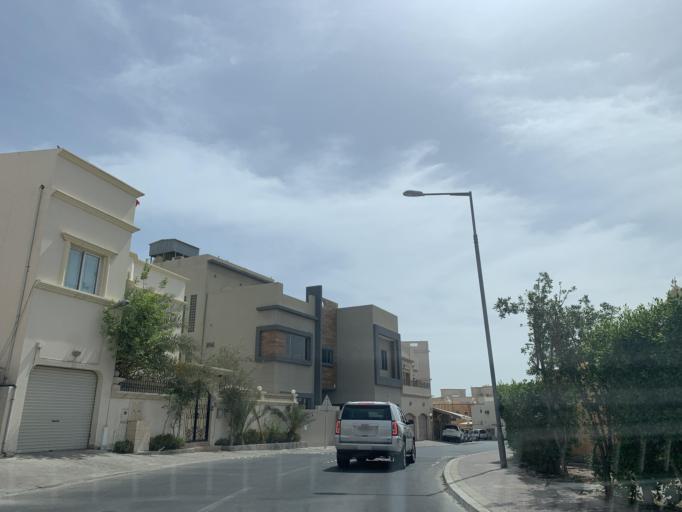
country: BH
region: Northern
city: Ar Rifa'
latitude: 26.1398
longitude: 50.5746
